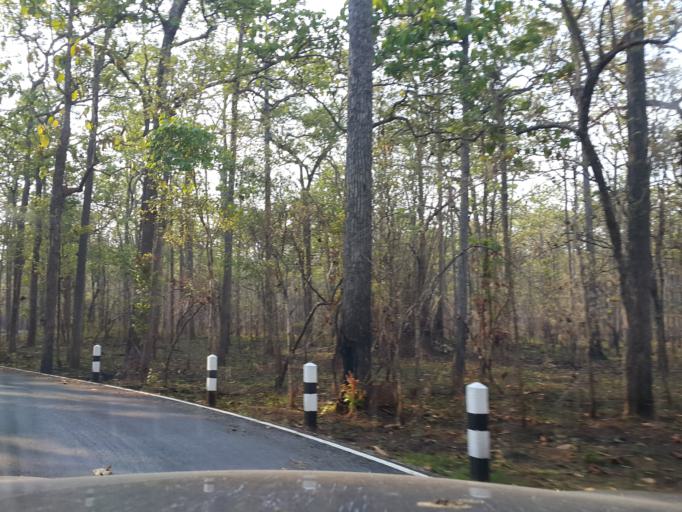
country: TH
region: Lamphun
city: Li
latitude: 17.6432
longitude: 98.8811
